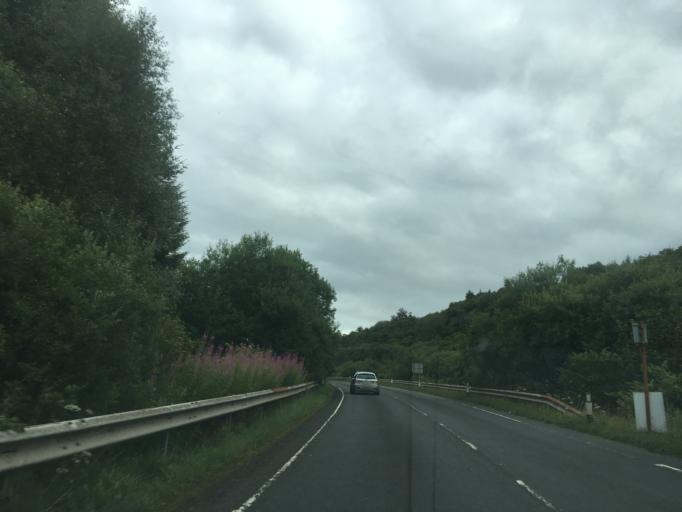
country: GB
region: Scotland
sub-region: Argyll and Bute
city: Oban
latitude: 56.3104
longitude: -5.4692
